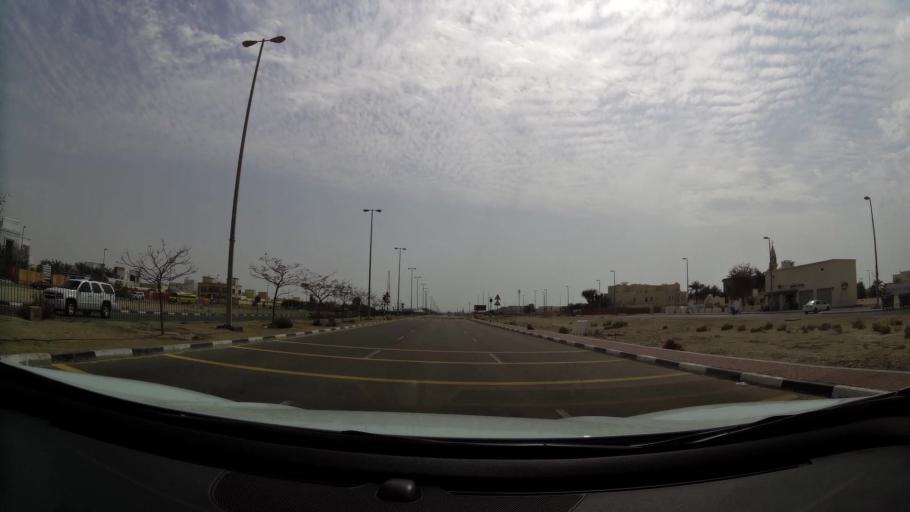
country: AE
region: Abu Dhabi
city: Abu Dhabi
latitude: 24.5576
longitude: 54.6856
